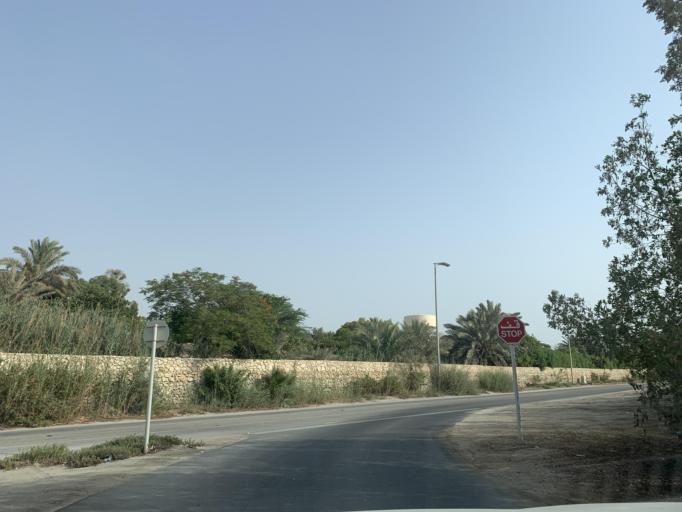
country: BH
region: Manama
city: Jidd Hafs
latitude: 26.2203
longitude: 50.4561
